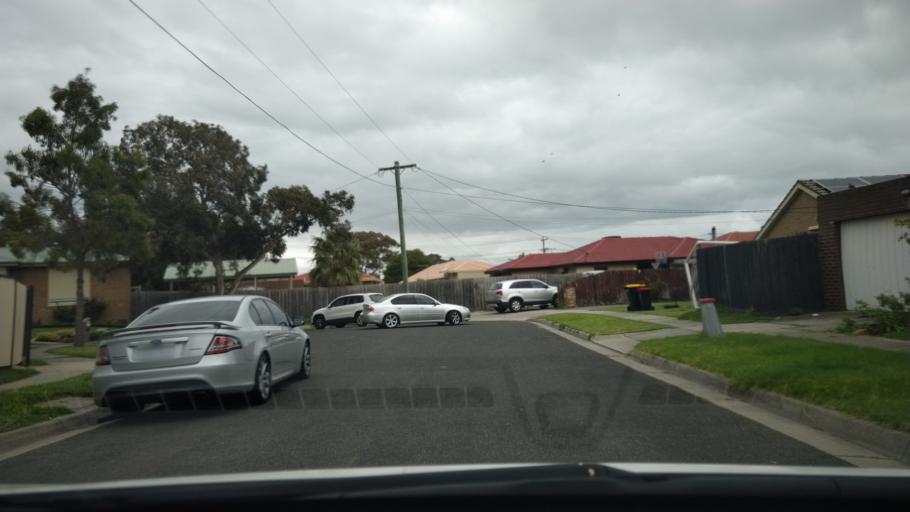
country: AU
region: Victoria
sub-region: Greater Dandenong
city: Keysborough
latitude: -37.9836
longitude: 145.1593
